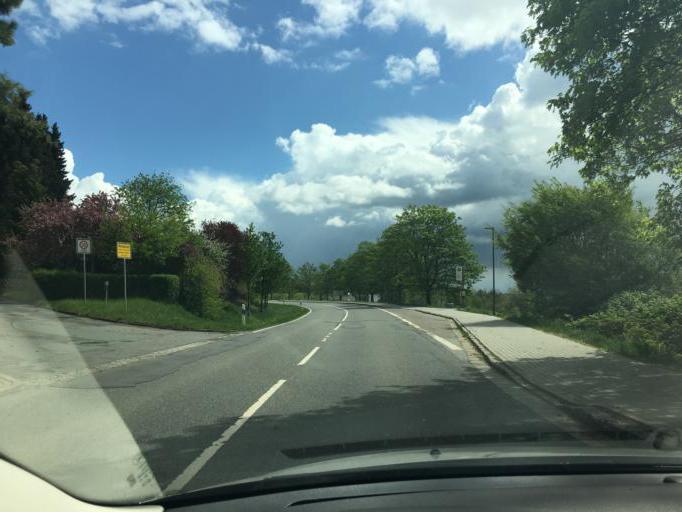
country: DE
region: Saxony
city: Hohenstein-Ernstthal
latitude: 50.8060
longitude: 12.7425
